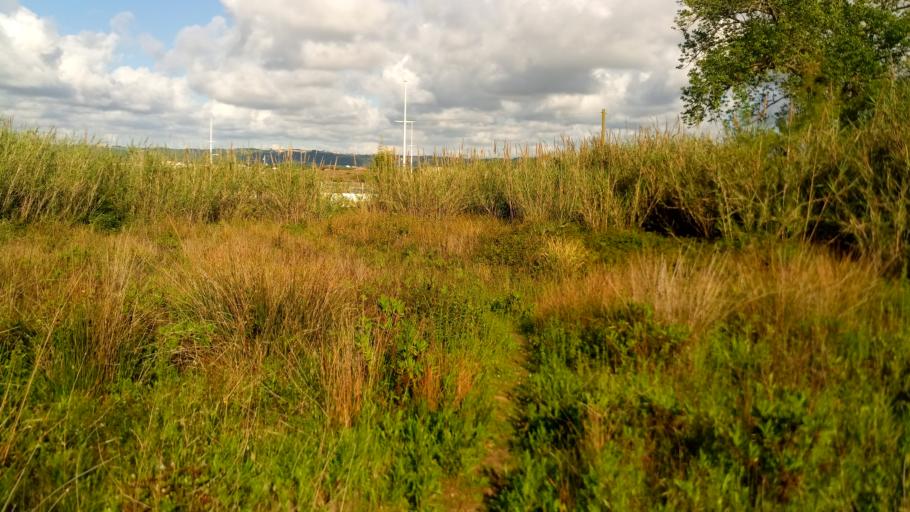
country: PT
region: Leiria
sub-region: Caldas da Rainha
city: Caldas da Rainha
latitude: 39.5006
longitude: -9.1527
